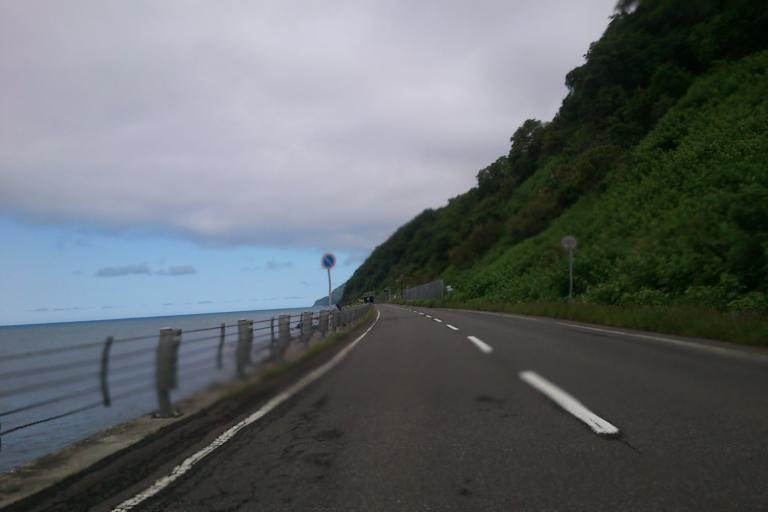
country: JP
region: Hokkaido
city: Ishikari
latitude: 43.4330
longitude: 141.4194
